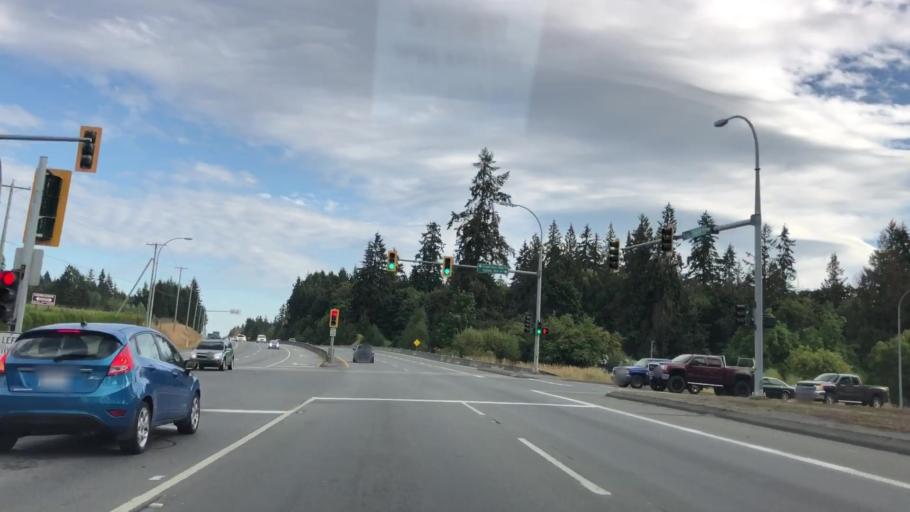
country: CA
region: British Columbia
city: Duncan
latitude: 48.7079
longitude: -123.6079
